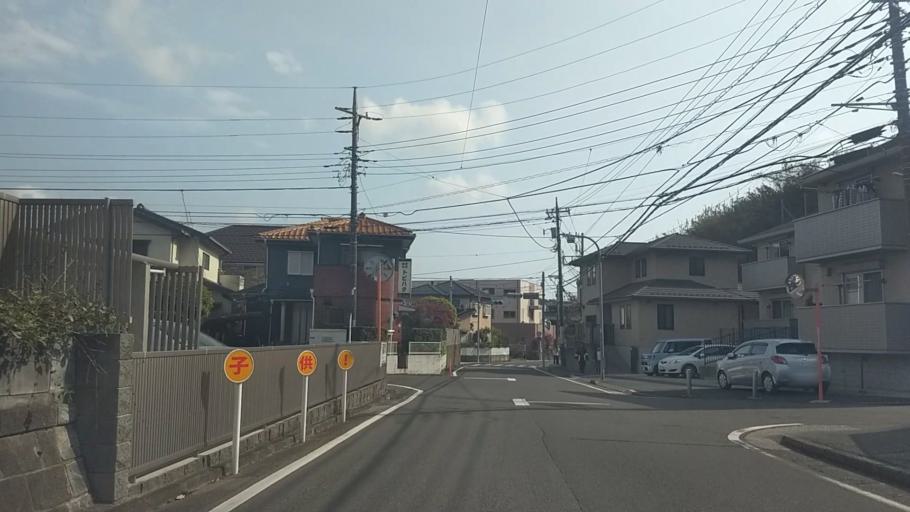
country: JP
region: Kanagawa
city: Kamakura
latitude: 35.3751
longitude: 139.5546
